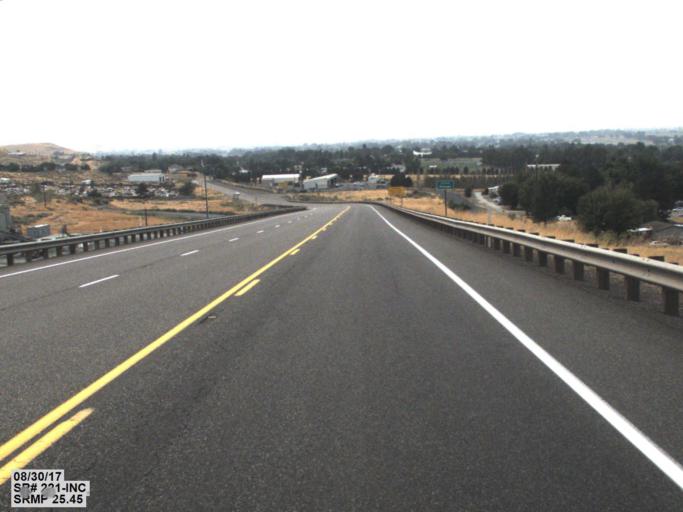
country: US
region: Washington
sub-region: Benton County
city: Prosser
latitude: 46.2080
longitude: -119.7359
